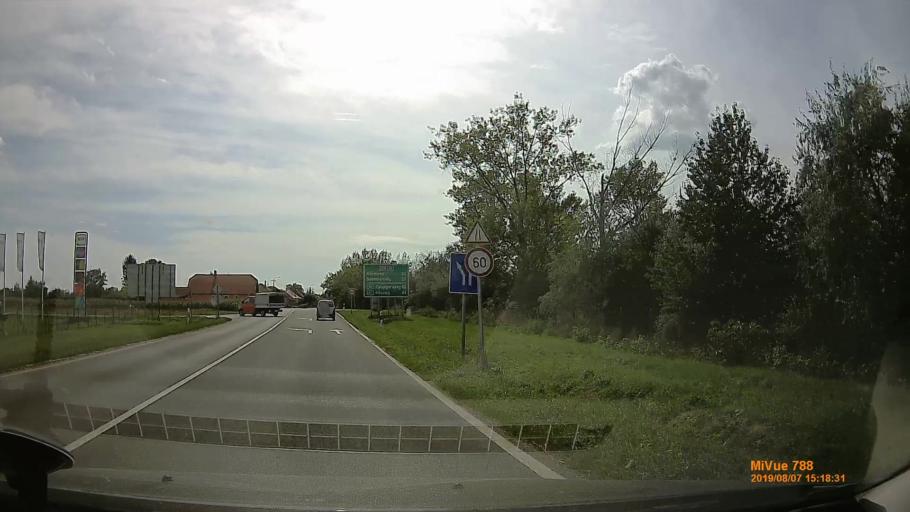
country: HU
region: Vas
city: Sarvar
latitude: 47.3587
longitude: 16.8926
